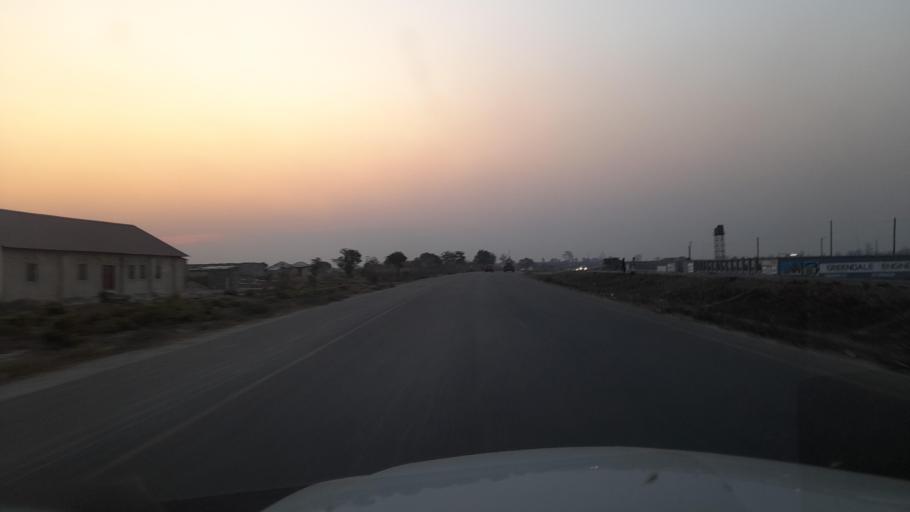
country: ZM
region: Copperbelt
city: Kitwe
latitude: -12.7627
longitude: 28.1693
